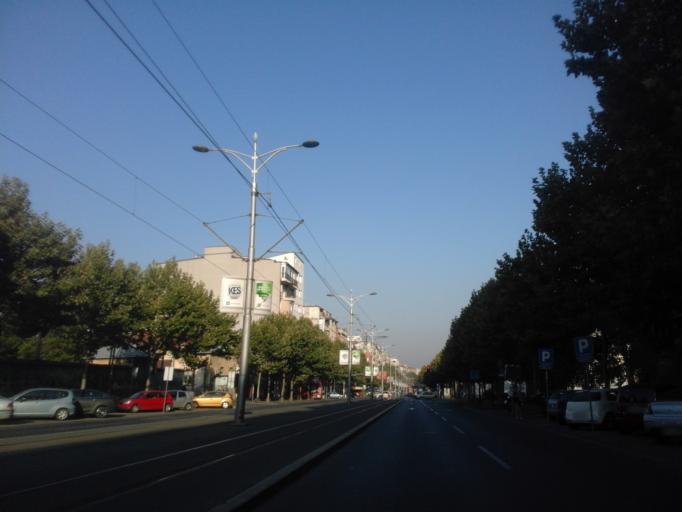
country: RS
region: Central Serbia
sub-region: Belgrade
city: Vracar
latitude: 44.8029
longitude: 20.4818
